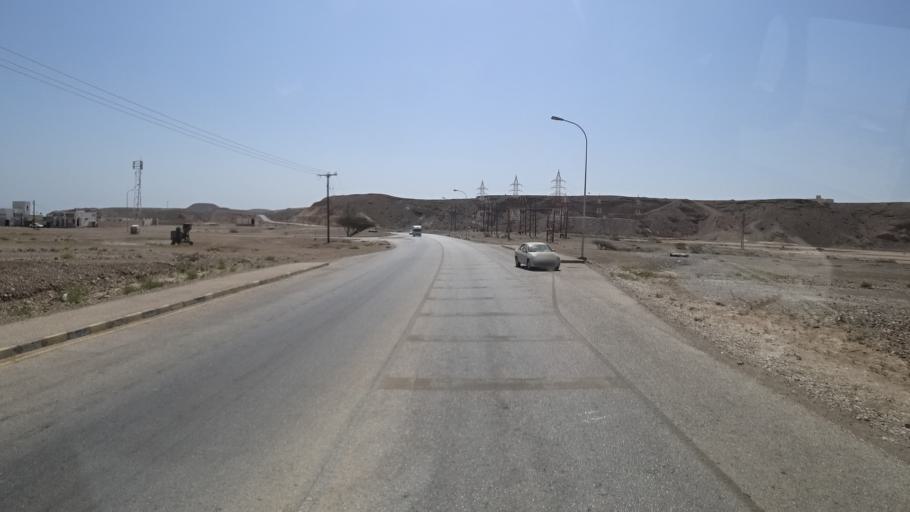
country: OM
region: Ash Sharqiyah
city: Sur
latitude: 22.5422
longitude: 59.5058
